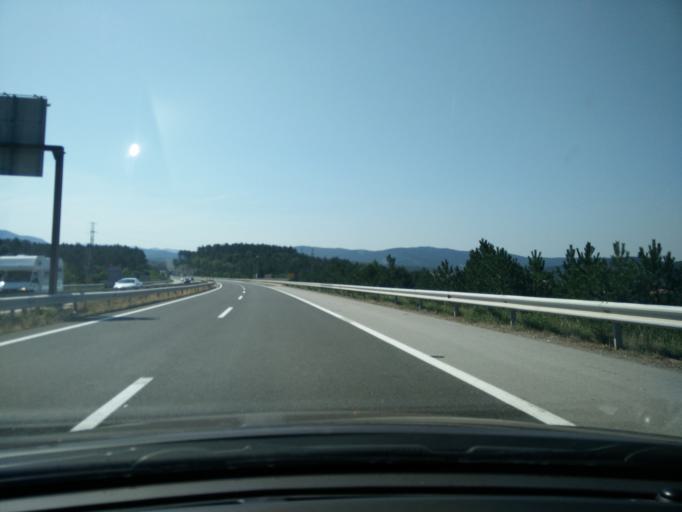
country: SI
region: Divaca
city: Divaca
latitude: 45.6930
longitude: 13.9787
